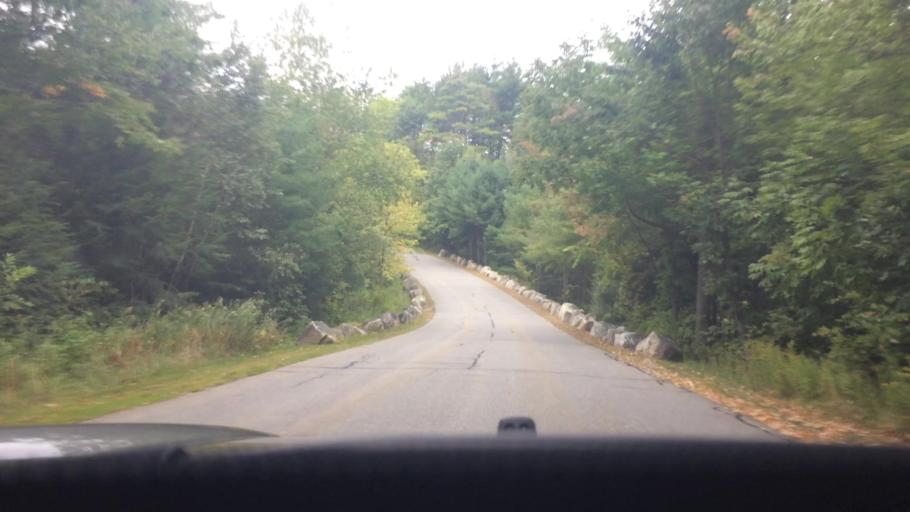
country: US
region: Maine
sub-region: Kennebec County
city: Augusta
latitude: 44.3505
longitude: -69.7916
